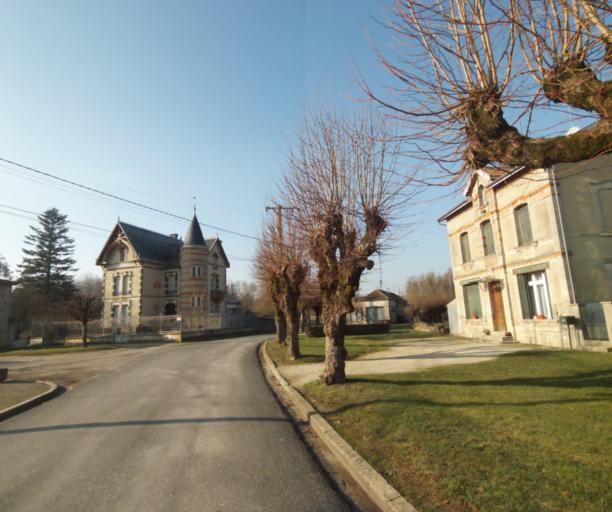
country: FR
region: Champagne-Ardenne
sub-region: Departement de la Haute-Marne
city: Wassy
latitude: 48.4715
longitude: 4.9696
